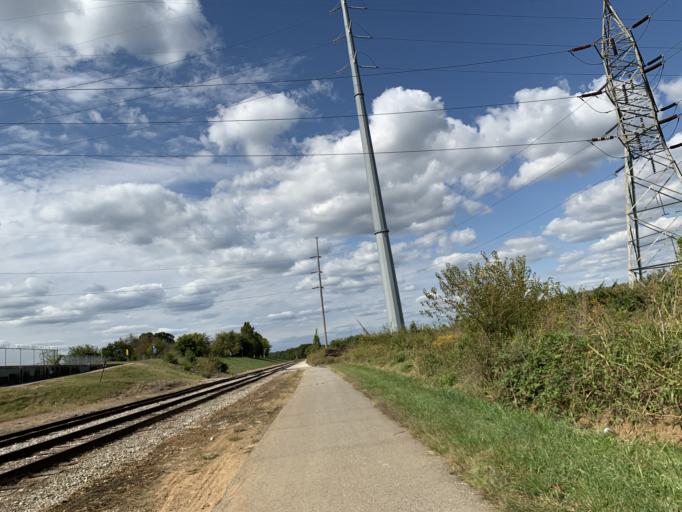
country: US
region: Kentucky
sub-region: Jefferson County
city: Louisville
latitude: 38.2710
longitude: -85.7802
